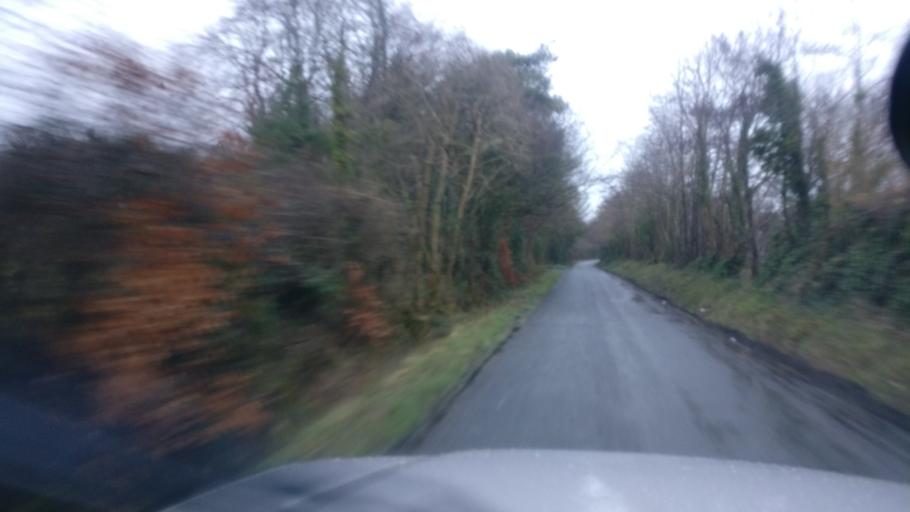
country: IE
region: Connaught
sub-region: County Galway
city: Ballinasloe
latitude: 53.3209
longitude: -8.3793
